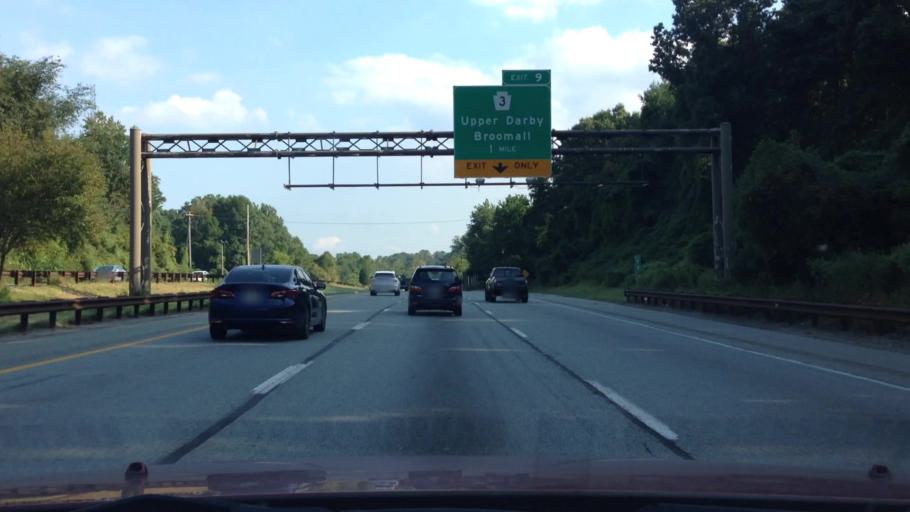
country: US
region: Pennsylvania
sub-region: Delaware County
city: Broomall
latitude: 39.9950
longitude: -75.3471
